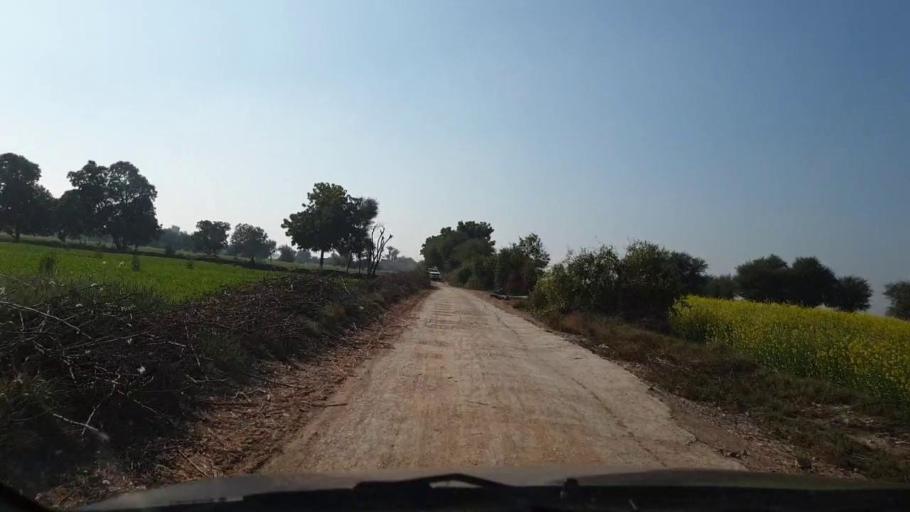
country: PK
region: Sindh
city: Sinjhoro
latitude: 25.9720
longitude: 68.7431
